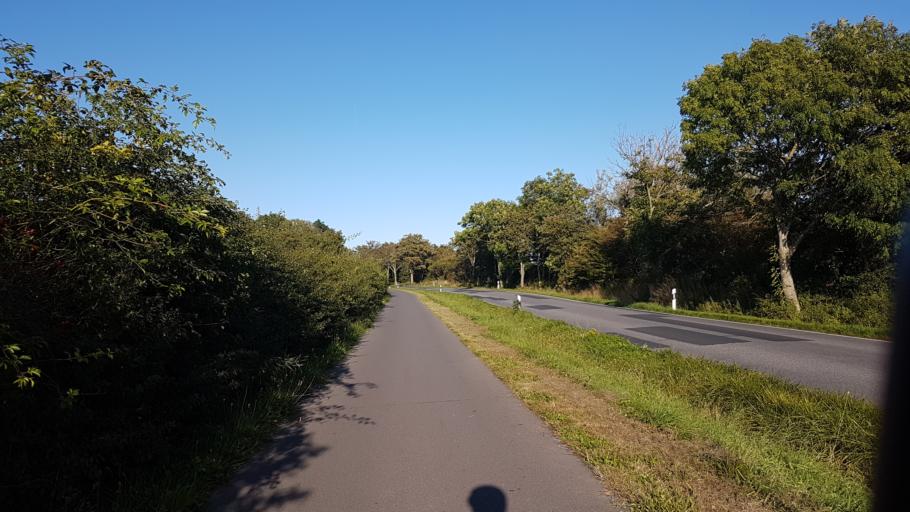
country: DE
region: Mecklenburg-Vorpommern
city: Dranske
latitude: 54.6393
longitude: 13.2543
